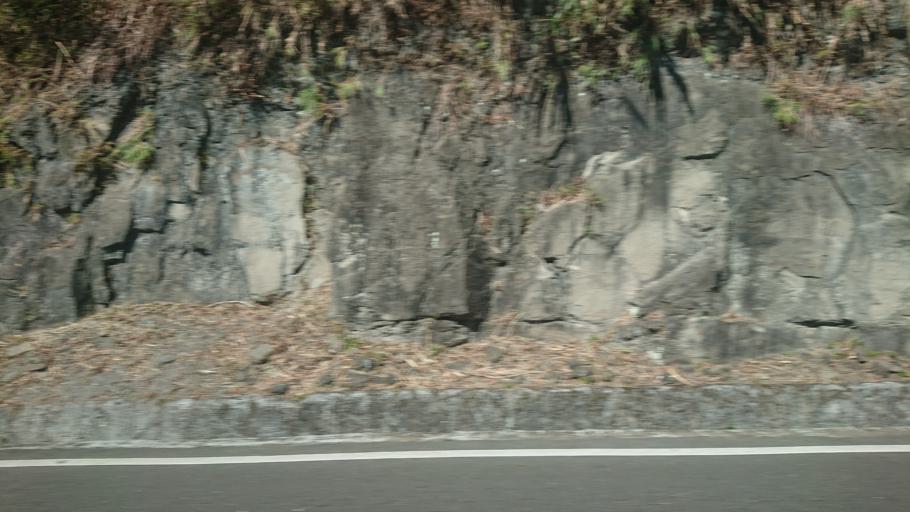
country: TW
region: Taiwan
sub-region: Chiayi
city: Jiayi Shi
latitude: 23.4650
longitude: 120.7284
